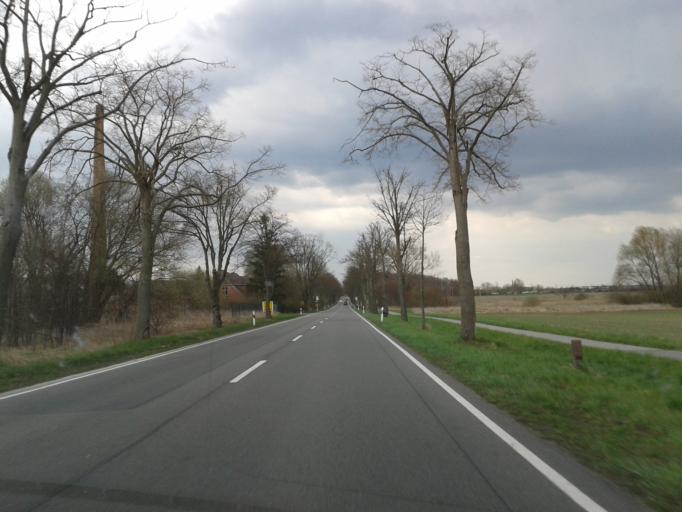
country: DE
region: Saxony-Anhalt
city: Salzwedel
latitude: 52.8645
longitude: 11.1051
